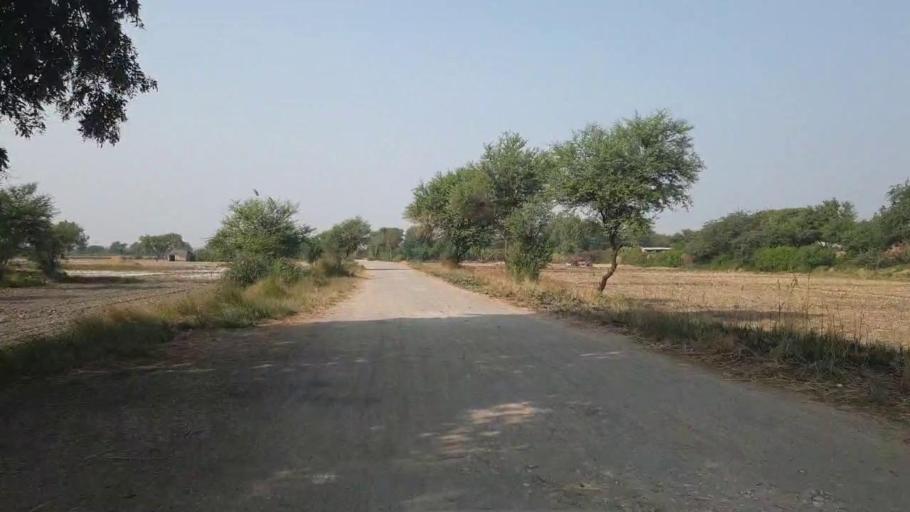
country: PK
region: Sindh
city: Tando Muhammad Khan
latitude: 25.0827
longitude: 68.3420
